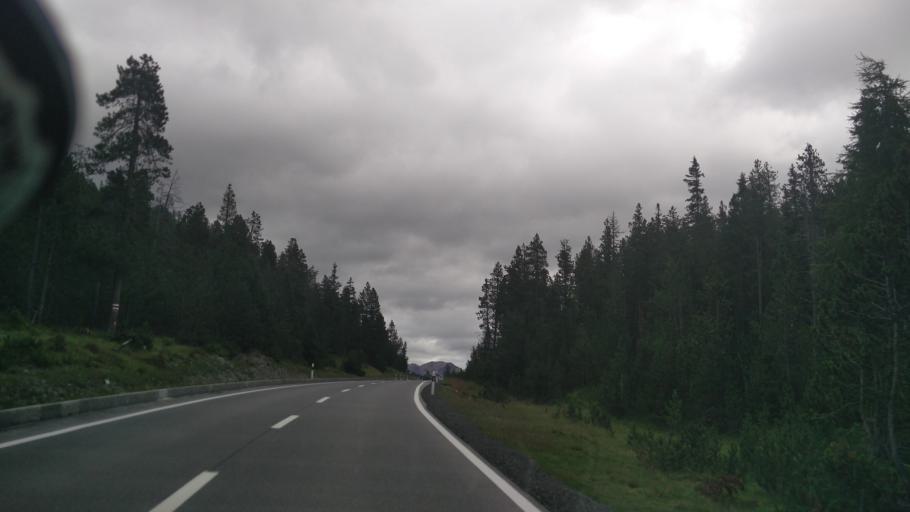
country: CH
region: Grisons
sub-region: Inn District
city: Zernez
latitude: 46.6814
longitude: 10.1579
